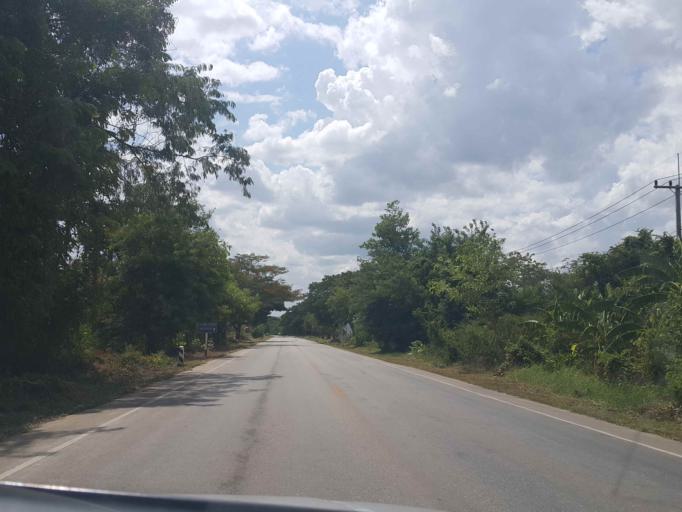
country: TH
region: Sukhothai
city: Thung Saliam
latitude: 17.3317
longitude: 99.6205
